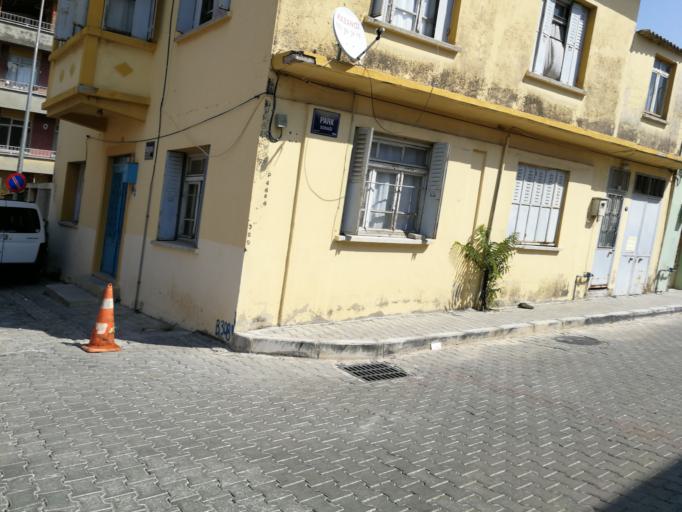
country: TR
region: Izmir
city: Urla
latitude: 38.3226
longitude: 26.7689
